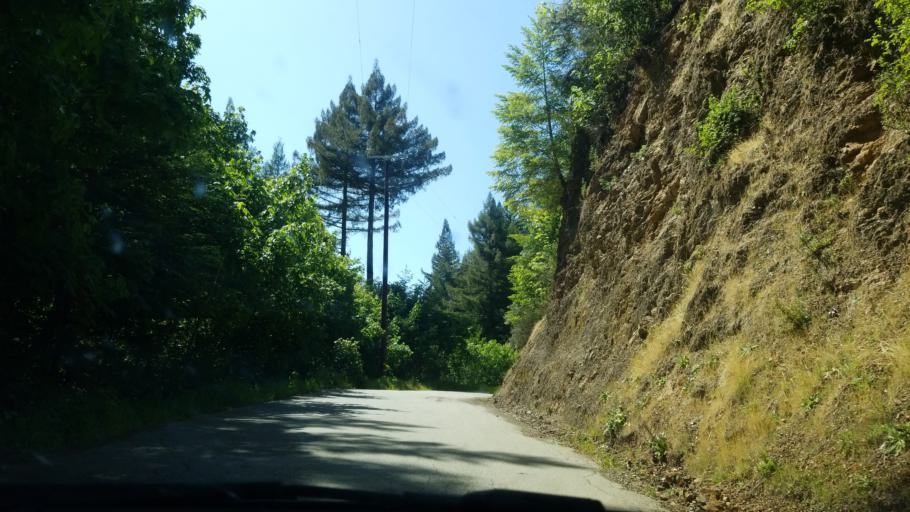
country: US
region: California
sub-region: Santa Cruz County
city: Day Valley
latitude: 37.0839
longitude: -121.8541
